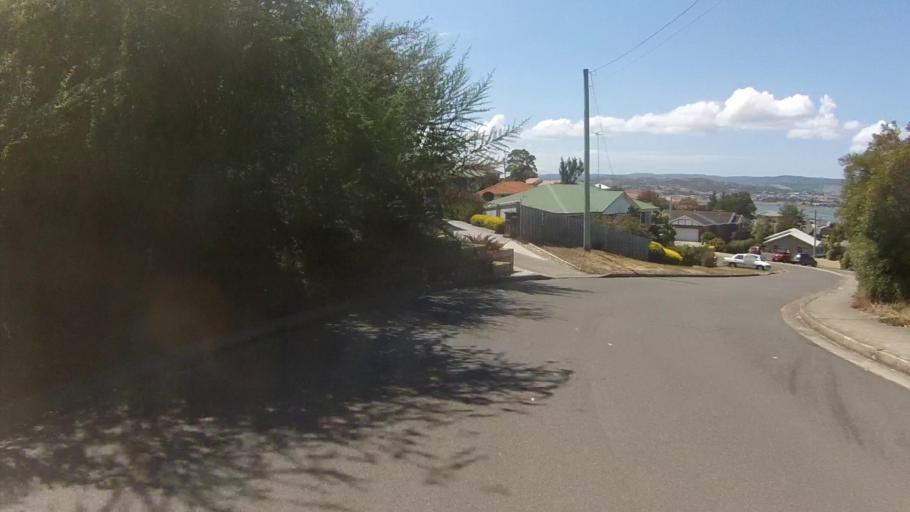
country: AU
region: Tasmania
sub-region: Sorell
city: Sorell
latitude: -42.7991
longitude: 147.5338
